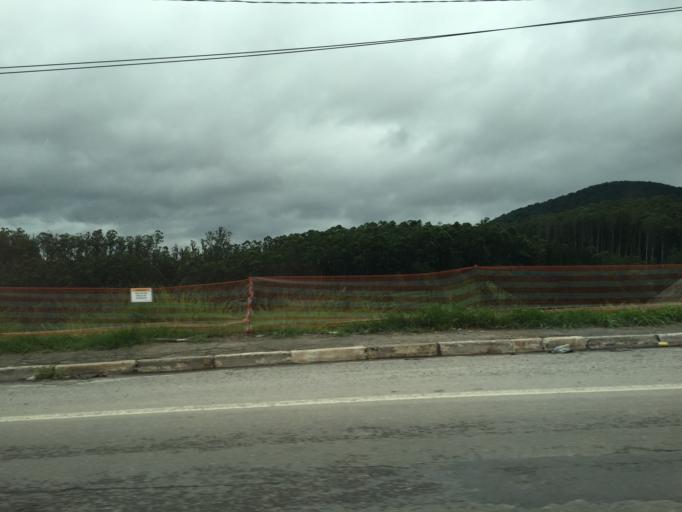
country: BR
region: Sao Paulo
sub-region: Caieiras
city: Caieiras
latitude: -23.4163
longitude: -46.7314
